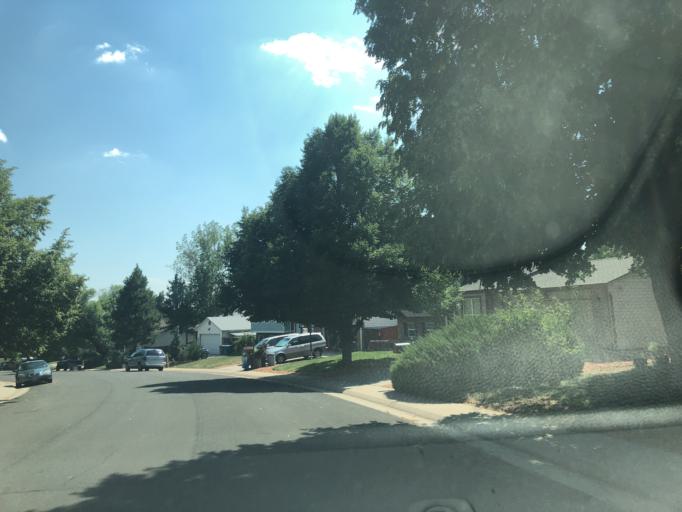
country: US
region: Colorado
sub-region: Arapahoe County
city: Dove Valley
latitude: 39.6367
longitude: -104.7681
